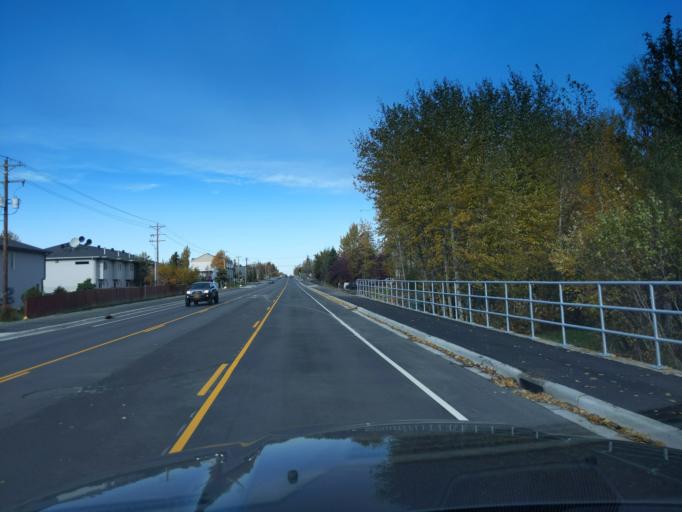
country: US
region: Alaska
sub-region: Anchorage Municipality
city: Anchorage
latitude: 61.1424
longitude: -149.9518
